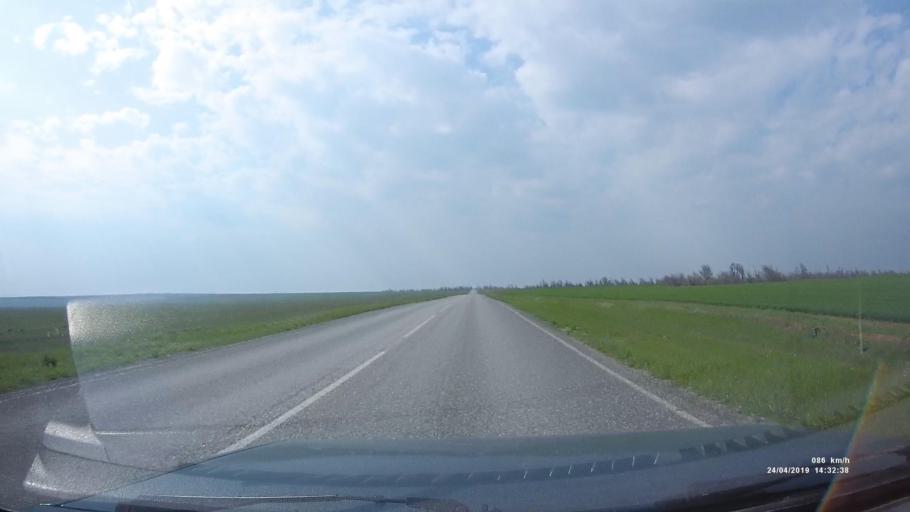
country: RU
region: Kalmykiya
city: Arshan'
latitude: 46.3663
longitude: 43.9660
